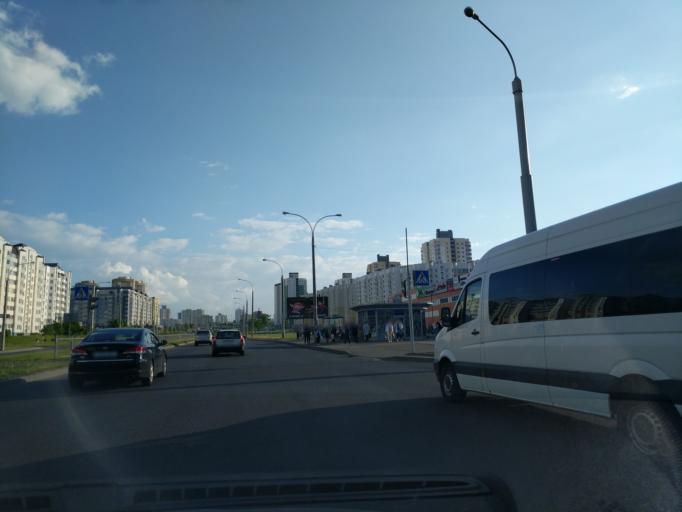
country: BY
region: Minsk
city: Zhdanovichy
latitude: 53.9270
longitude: 27.4423
